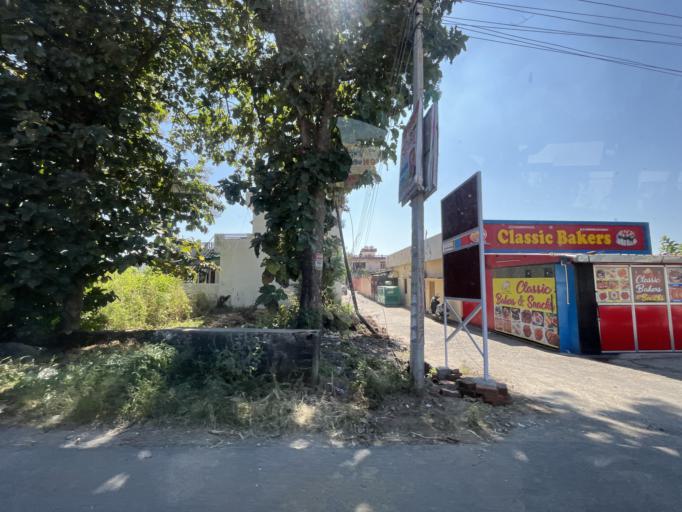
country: IN
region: Uttarakhand
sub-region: Naini Tal
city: Haldwani
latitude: 29.2136
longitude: 79.4768
